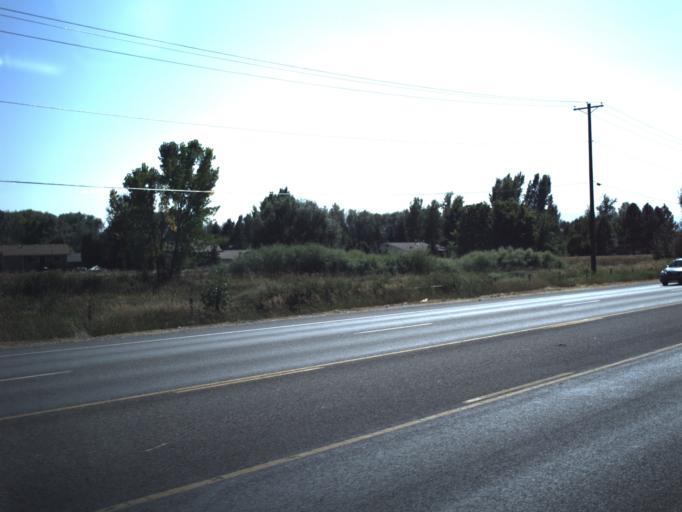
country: US
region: Utah
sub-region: Cache County
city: River Heights
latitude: 41.7068
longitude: -111.8471
